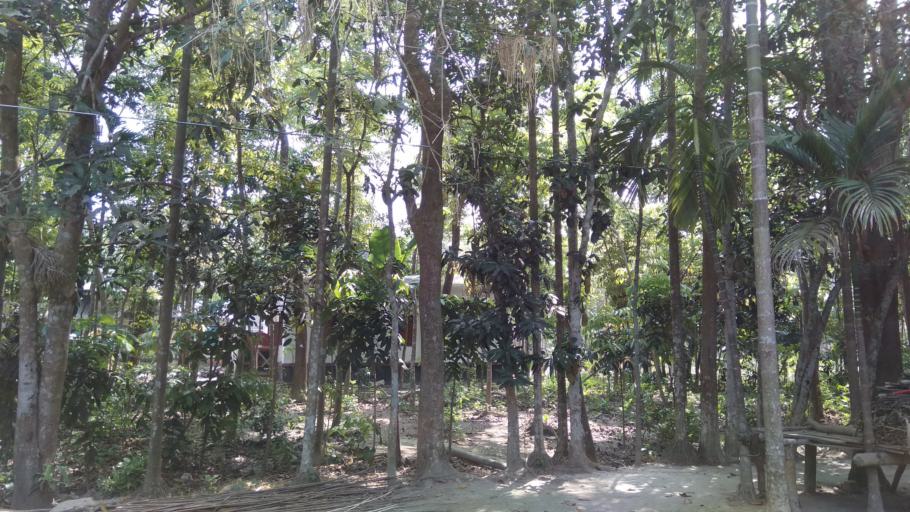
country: BD
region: Barisal
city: Gaurnadi
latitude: 22.9189
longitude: 90.3790
